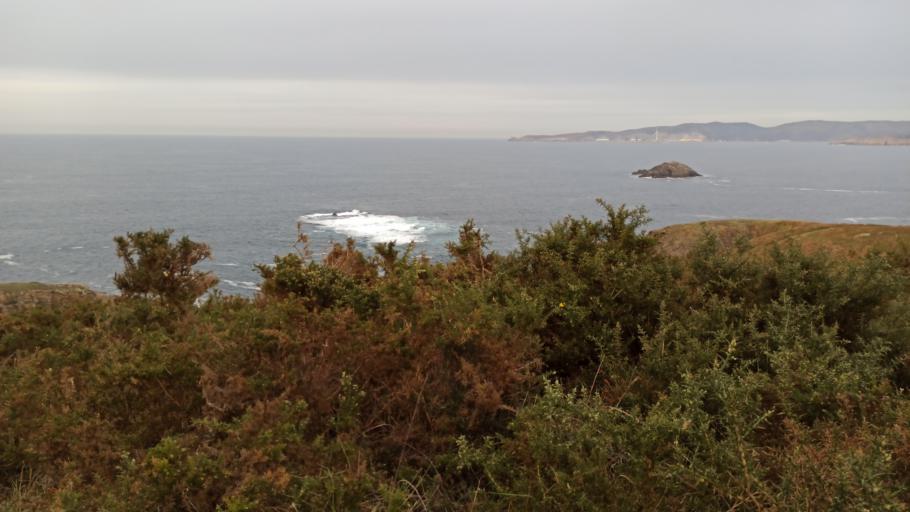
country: ES
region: Galicia
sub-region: Provincia da Coruna
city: A Coruna
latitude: 43.3972
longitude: -8.3375
